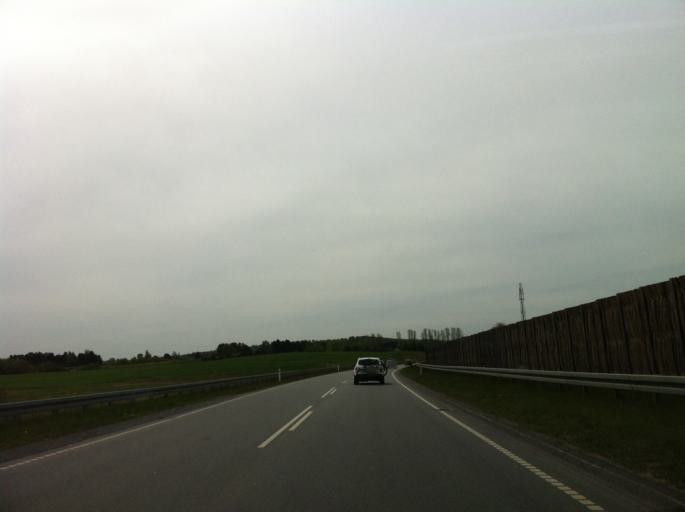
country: DK
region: Capital Region
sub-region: Frederikssund Kommune
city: Slangerup
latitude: 55.8857
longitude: 12.2052
